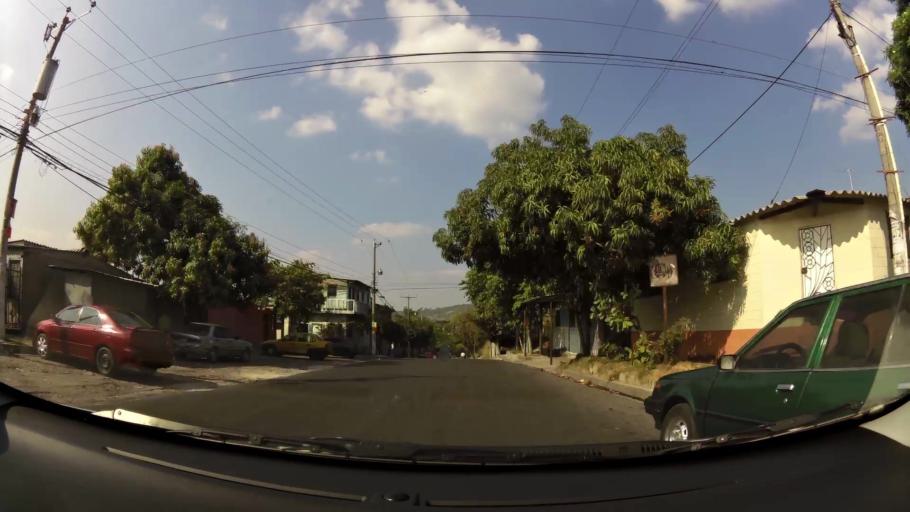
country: SV
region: San Salvador
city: Ilopango
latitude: 13.7202
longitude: -89.1060
